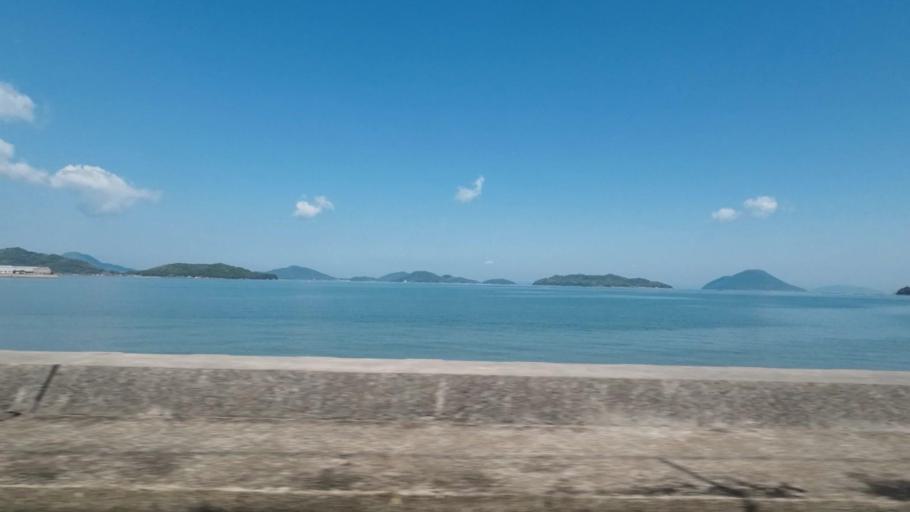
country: JP
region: Kagawa
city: Tadotsu
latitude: 34.2366
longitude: 133.7028
